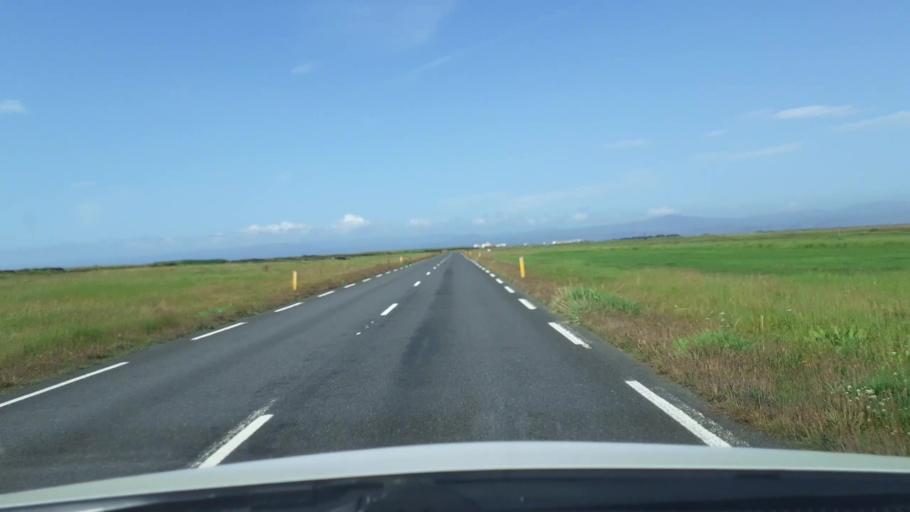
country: IS
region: South
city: Selfoss
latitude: 63.8439
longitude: -21.0877
